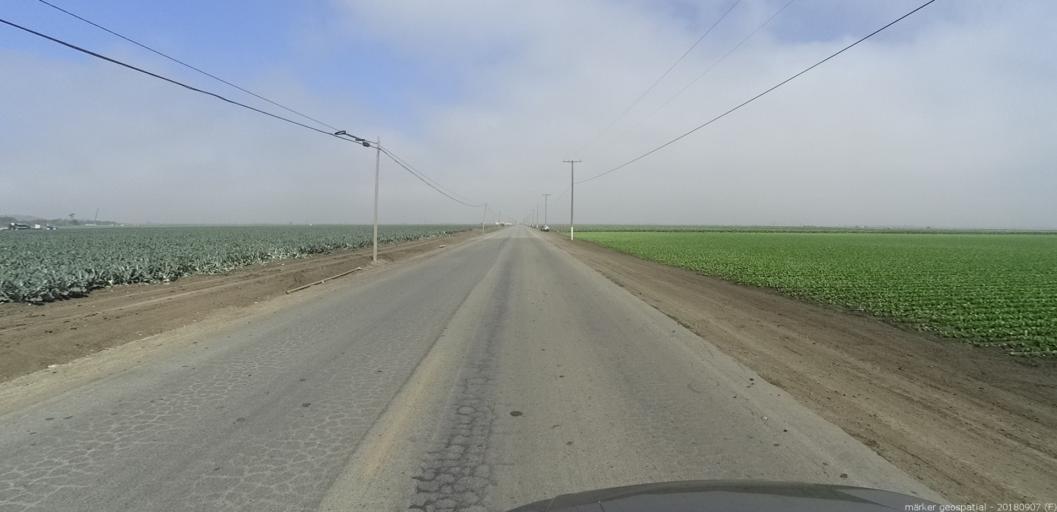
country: US
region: California
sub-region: Monterey County
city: Boronda
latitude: 36.7034
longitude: -121.7359
